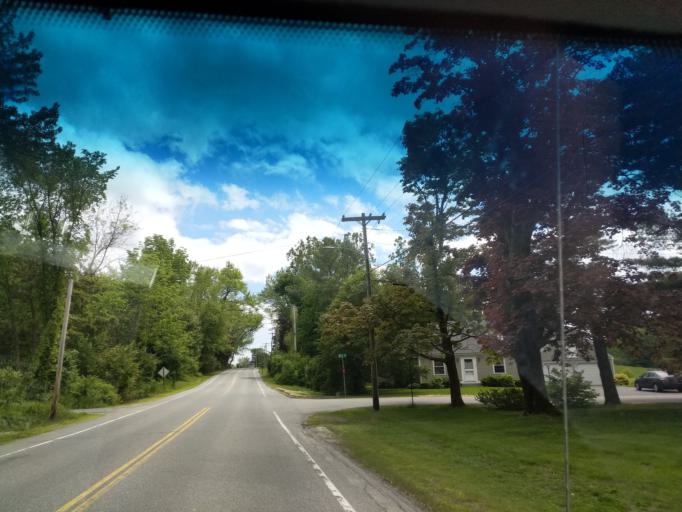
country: US
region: Maine
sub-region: Cumberland County
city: Falmouth
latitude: 43.7454
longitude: -70.2934
